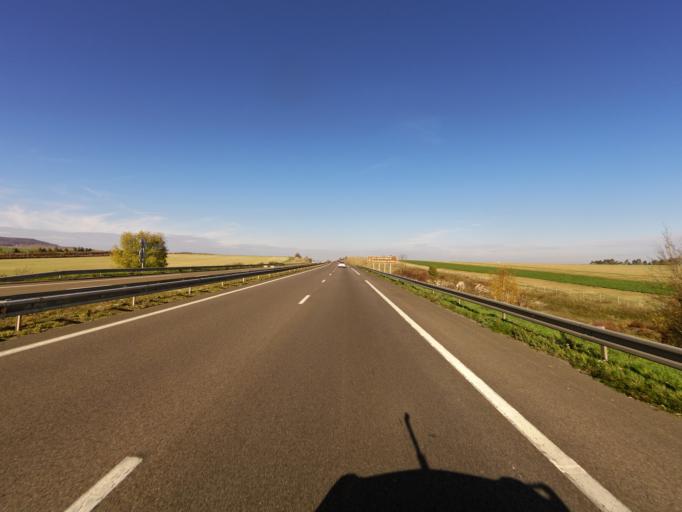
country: FR
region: Champagne-Ardenne
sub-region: Departement de la Marne
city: Verzy
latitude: 49.1407
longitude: 4.2159
